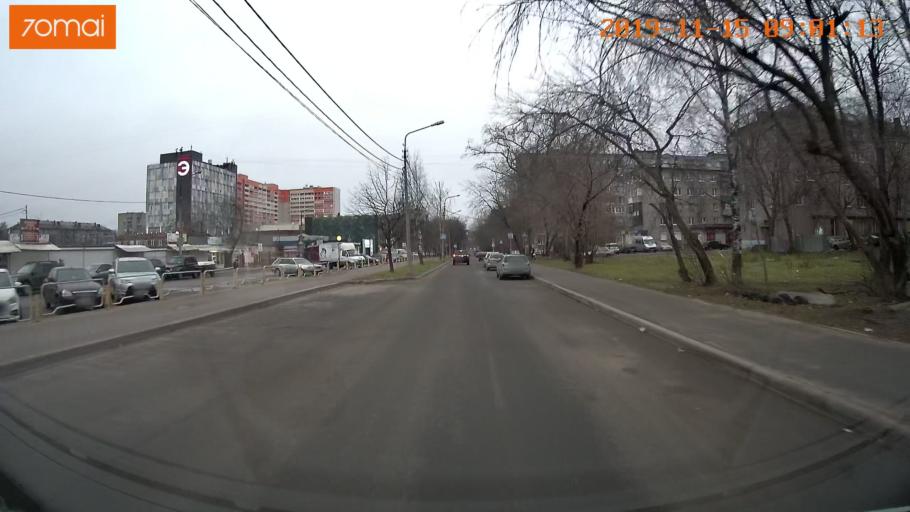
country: RU
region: Vologda
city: Cherepovets
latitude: 59.1311
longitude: 37.9253
